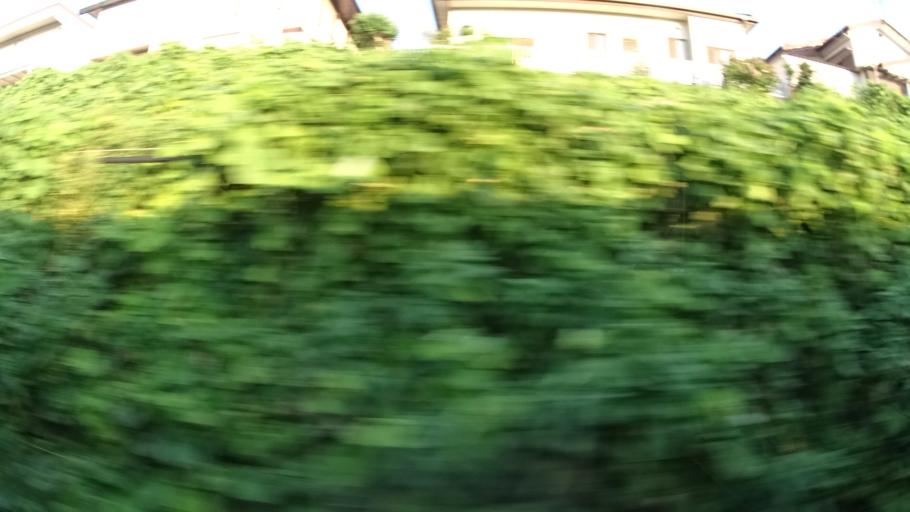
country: JP
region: Ibaraki
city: Naka
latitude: 36.0674
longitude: 140.1947
